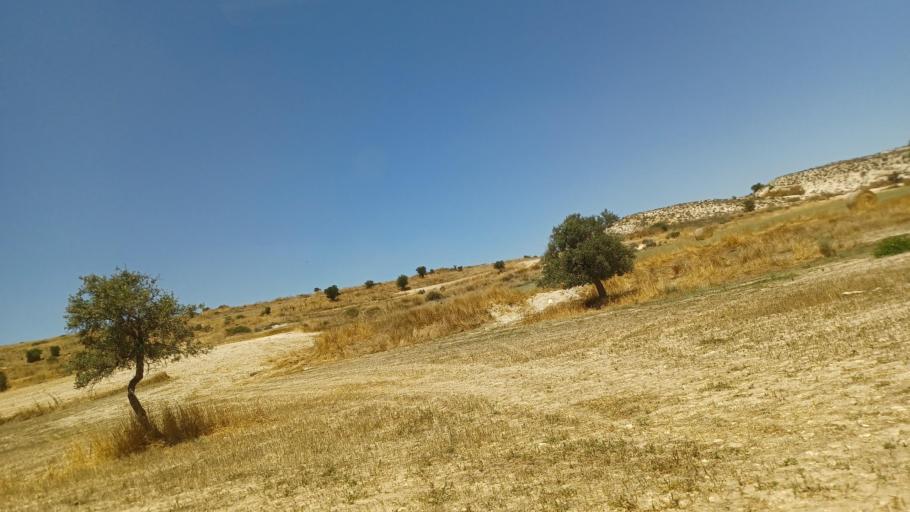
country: CY
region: Lefkosia
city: Lympia
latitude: 34.9912
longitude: 33.4907
